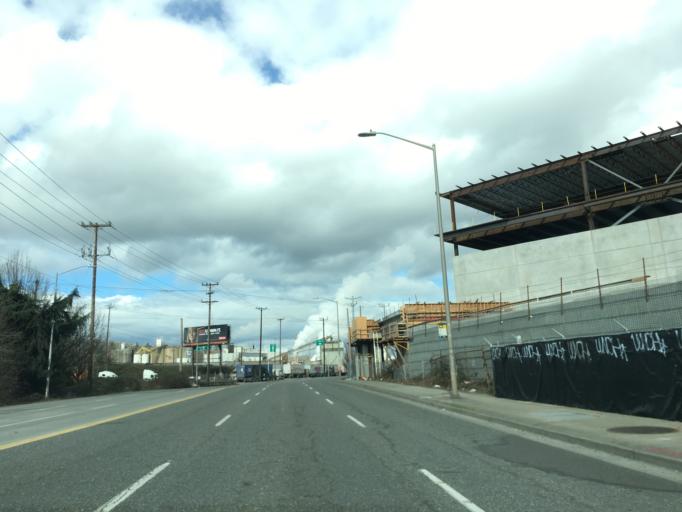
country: US
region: Washington
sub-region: King County
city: White Center
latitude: 47.5451
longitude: -122.3315
